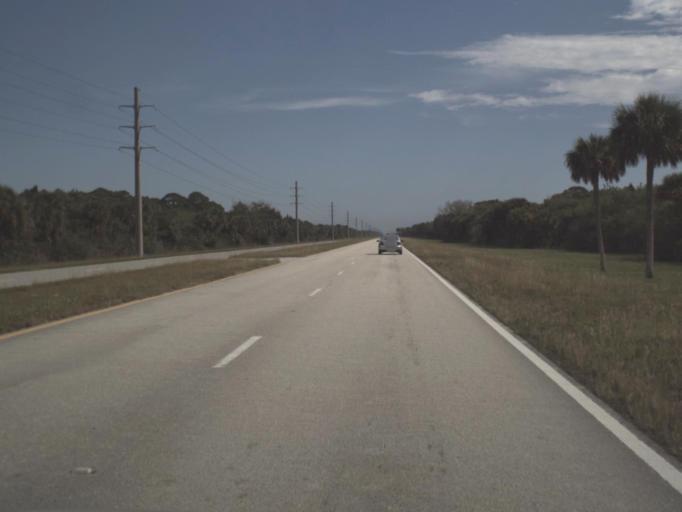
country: US
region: Florida
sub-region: Brevard County
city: Merritt Island
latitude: 28.5264
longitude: -80.7256
